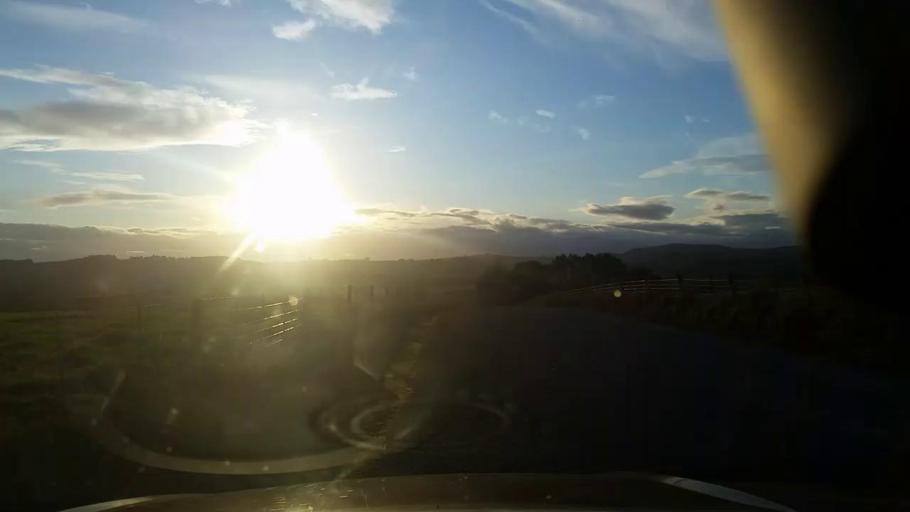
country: NZ
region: Southland
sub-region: Gore District
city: Gore
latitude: -45.9618
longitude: 168.9627
